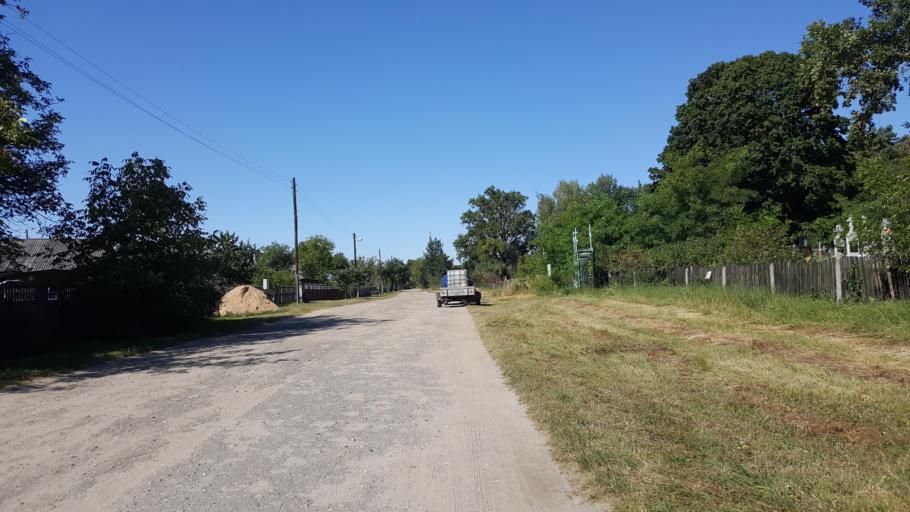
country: BY
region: Brest
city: Vysokaye
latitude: 52.2333
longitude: 23.5043
